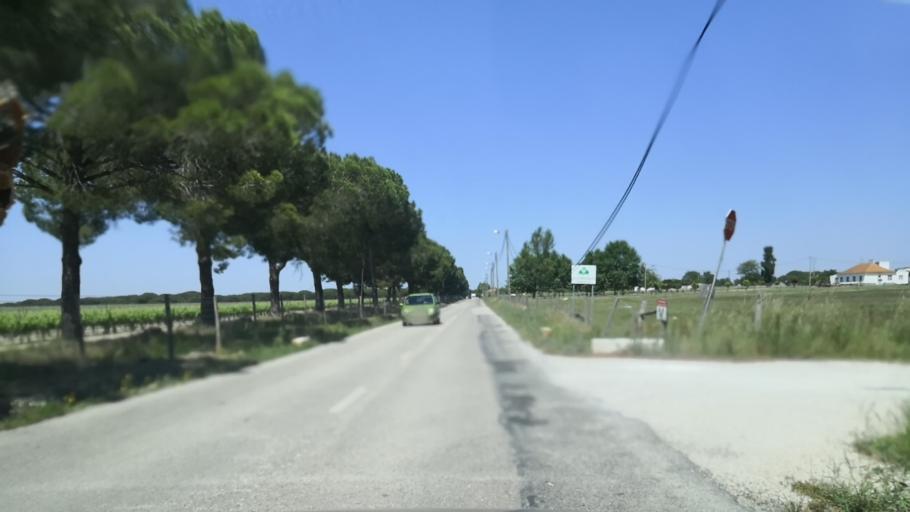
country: PT
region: Santarem
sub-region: Benavente
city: Poceirao
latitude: 38.6821
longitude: -8.7323
